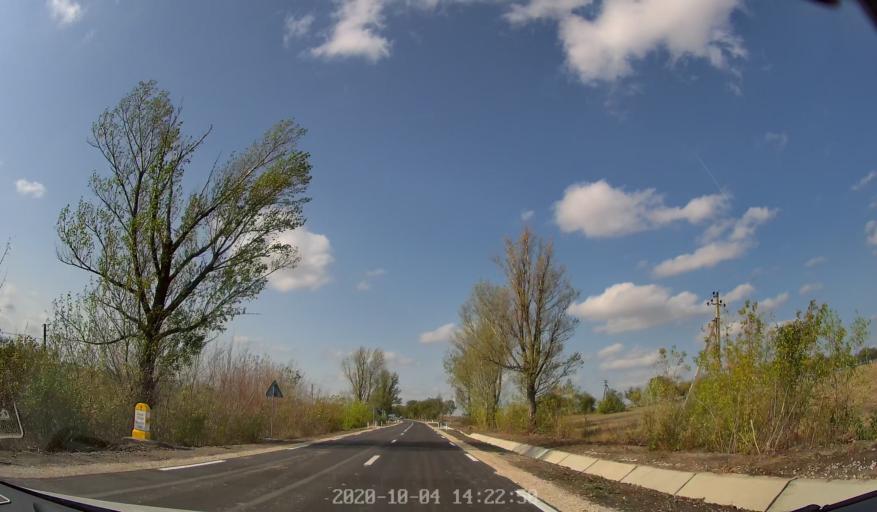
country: MD
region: Rezina
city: Saharna
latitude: 47.6030
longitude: 28.9440
